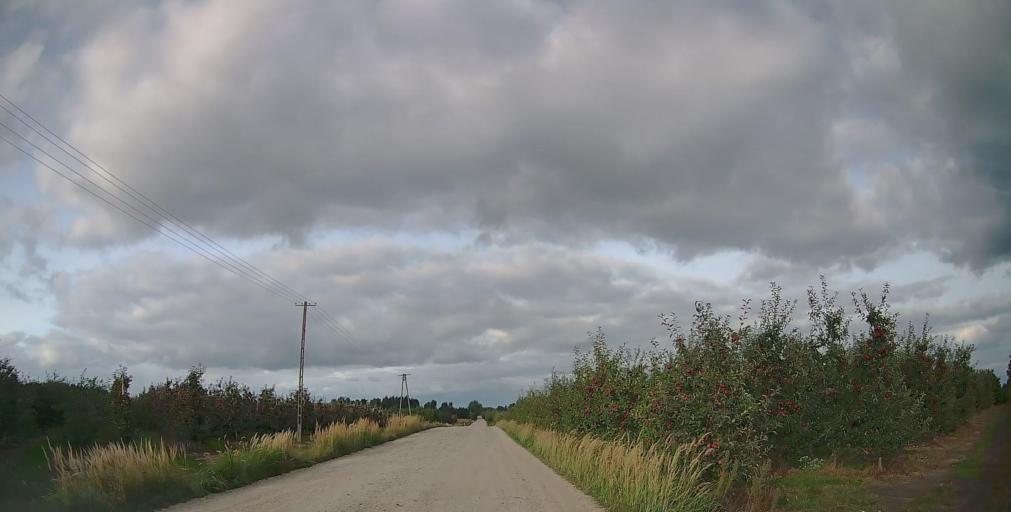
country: PL
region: Masovian Voivodeship
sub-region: Powiat grojecki
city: Jasieniec
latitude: 51.7732
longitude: 20.9209
